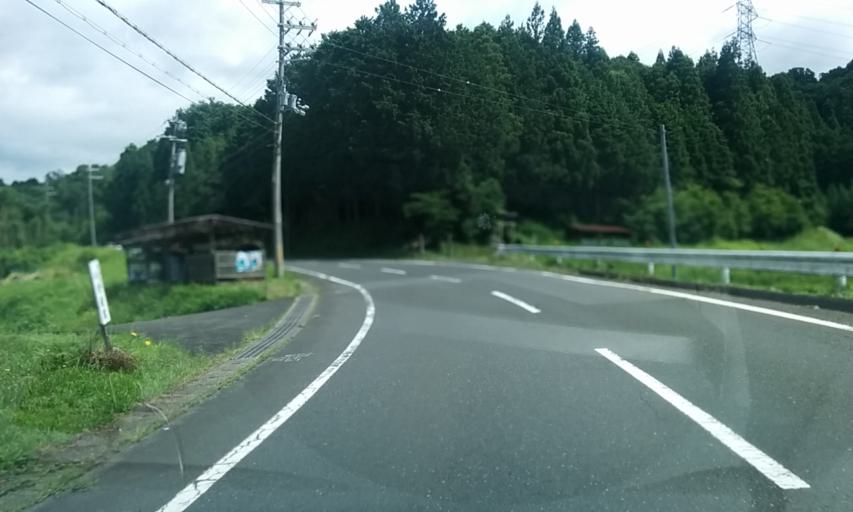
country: JP
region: Kyoto
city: Ayabe
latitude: 35.3528
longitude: 135.2712
